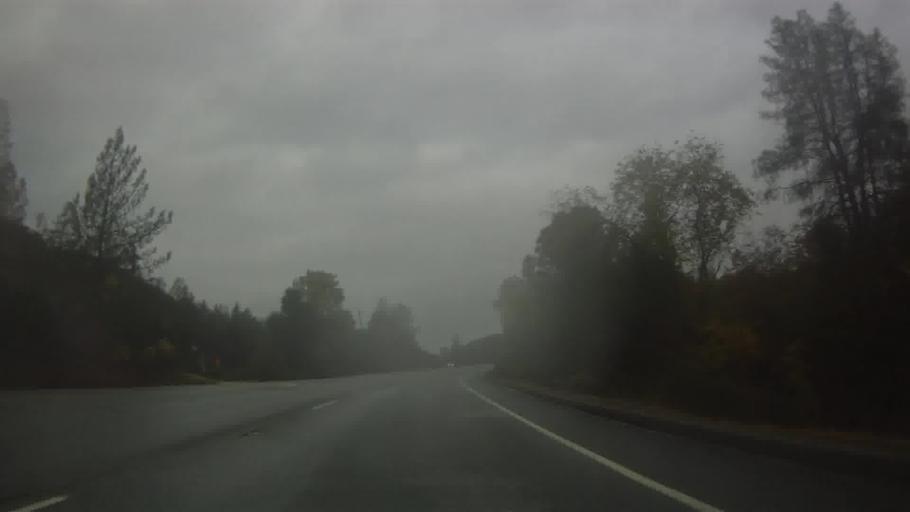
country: US
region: California
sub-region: Shasta County
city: Shasta
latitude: 40.5902
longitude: -122.4661
